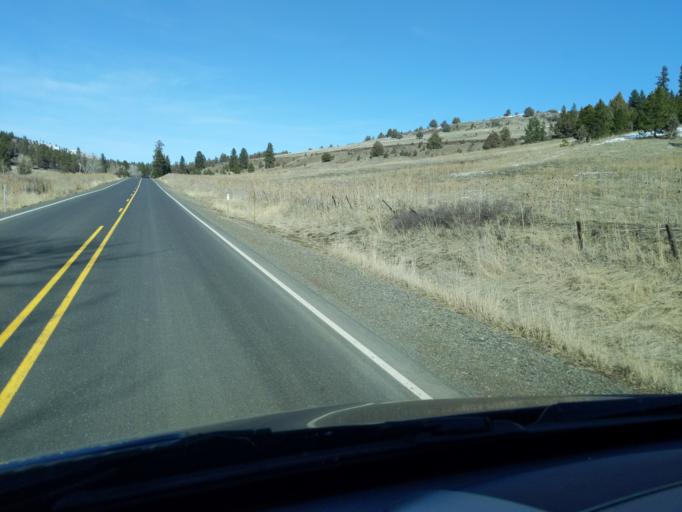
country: US
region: Oregon
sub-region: Grant County
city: John Day
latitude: 44.8559
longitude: -119.0291
